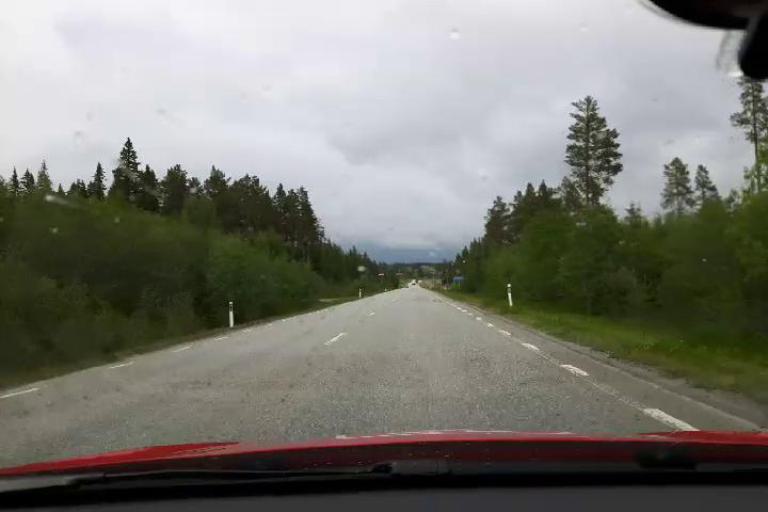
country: SE
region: Jaemtland
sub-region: Bergs Kommun
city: Hoverberg
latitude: 62.6788
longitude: 14.3860
